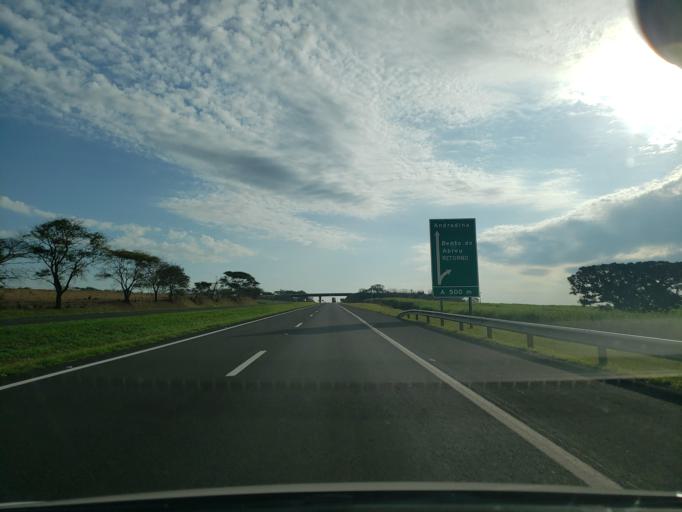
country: BR
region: Sao Paulo
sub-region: Valparaiso
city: Valparaiso
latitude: -21.2052
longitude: -50.7895
